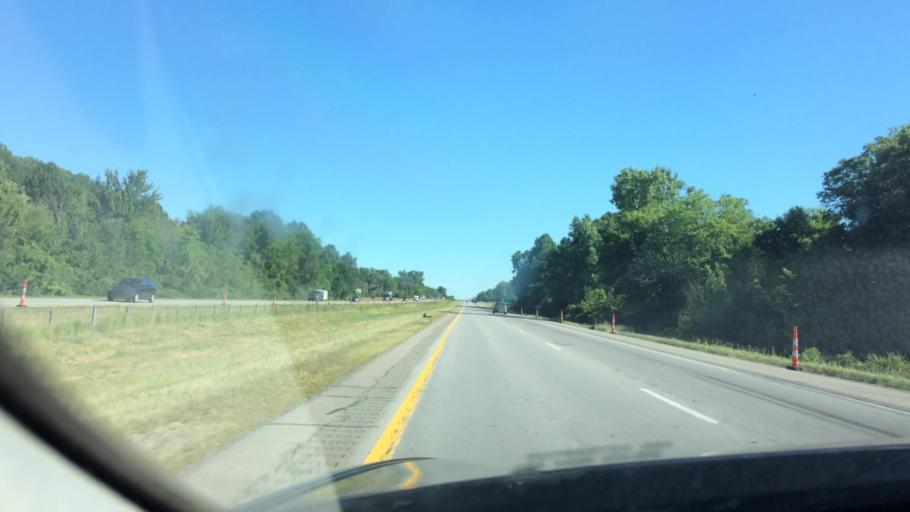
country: US
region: Michigan
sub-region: Washtenaw County
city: Milan
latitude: 42.1344
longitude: -83.6831
